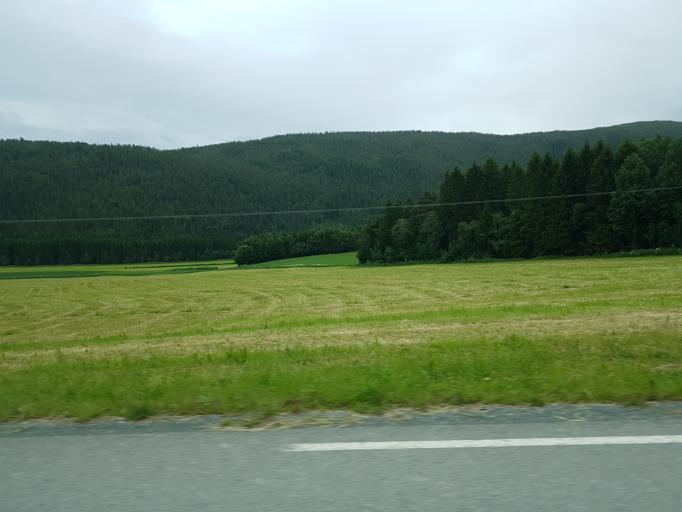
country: NO
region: Nord-Trondelag
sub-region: Levanger
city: Skogn
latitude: 63.6066
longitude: 11.0964
